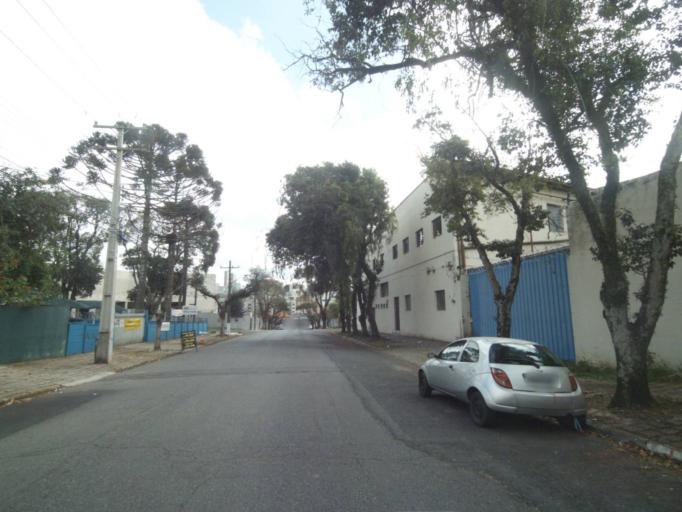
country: BR
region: Parana
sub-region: Curitiba
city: Curitiba
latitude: -25.4678
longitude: -49.2850
